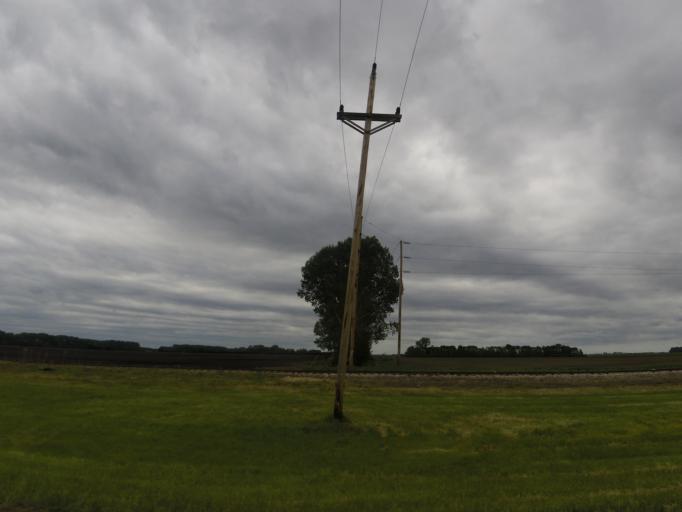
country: US
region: North Dakota
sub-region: Walsh County
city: Grafton
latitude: 48.5790
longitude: -97.4479
